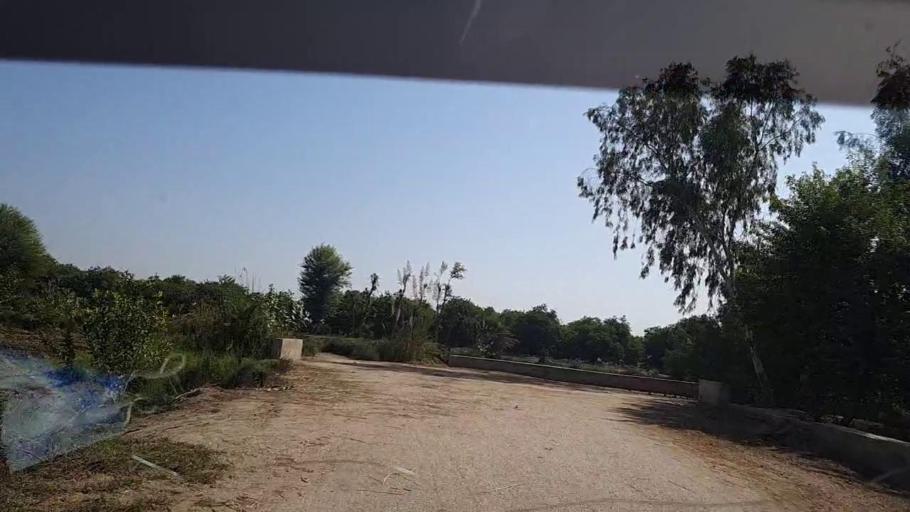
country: PK
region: Sindh
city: Larkana
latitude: 27.6022
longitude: 68.2678
